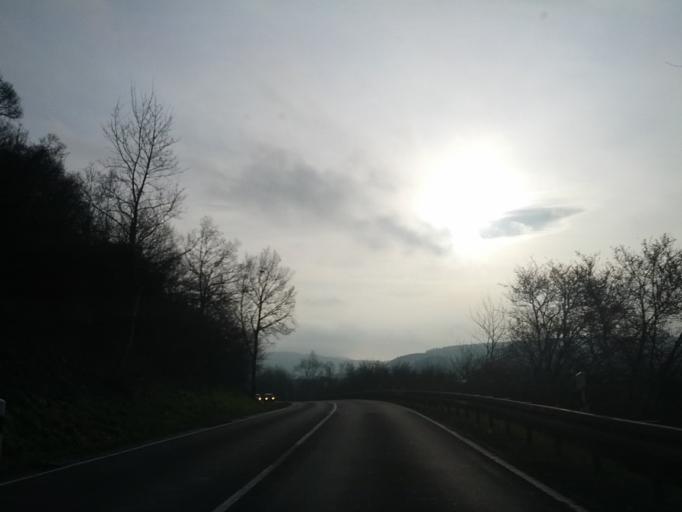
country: DE
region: Thuringia
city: Wasungen
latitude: 50.6715
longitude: 10.3549
